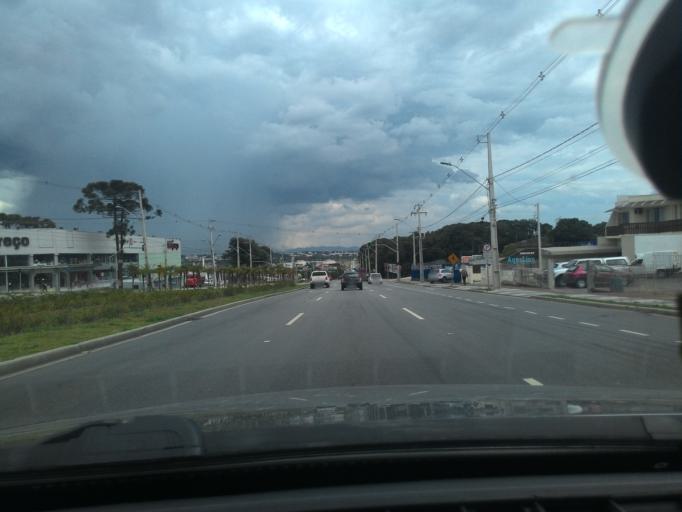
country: BR
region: Parana
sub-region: Sao Jose Dos Pinhais
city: Sao Jose dos Pinhais
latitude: -25.4909
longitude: -49.2157
